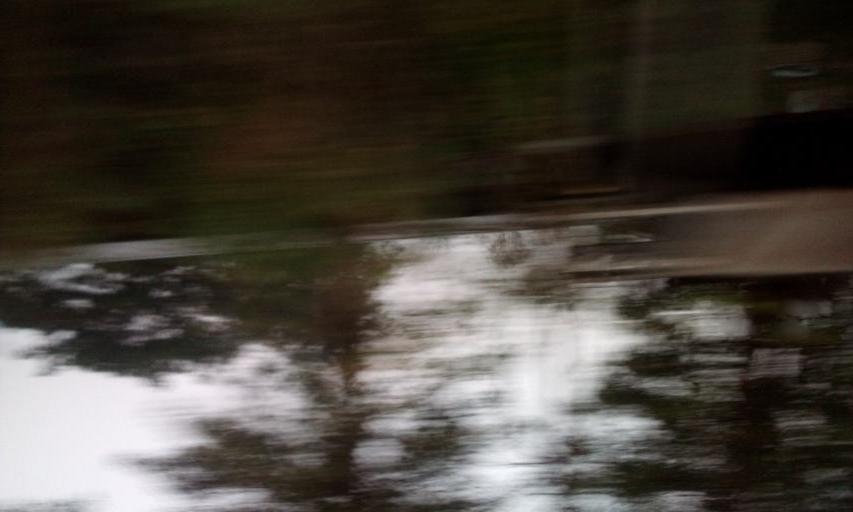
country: TH
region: Sing Buri
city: Sing Buri
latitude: 14.8306
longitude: 100.4025
